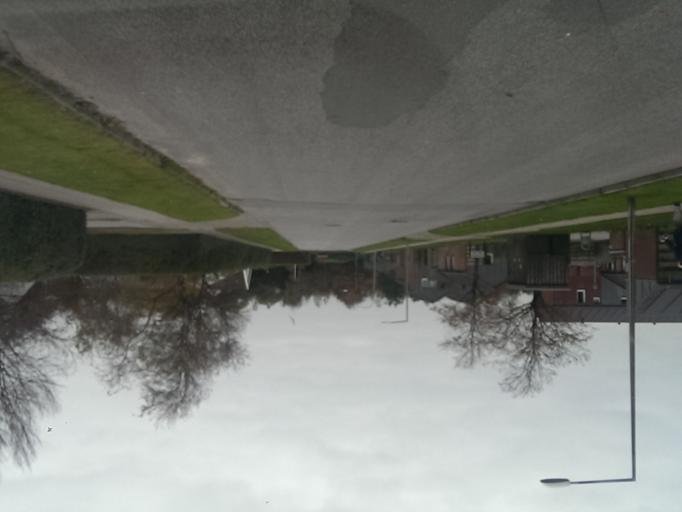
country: DK
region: South Denmark
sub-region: Esbjerg Kommune
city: Esbjerg
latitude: 55.5175
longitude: 8.4389
